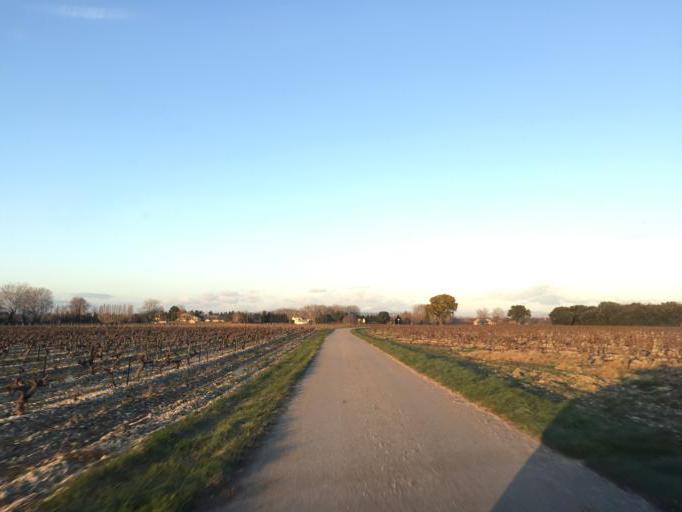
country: FR
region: Provence-Alpes-Cote d'Azur
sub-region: Departement du Vaucluse
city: Camaret-sur-Aigues
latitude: 44.1524
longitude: 4.8922
